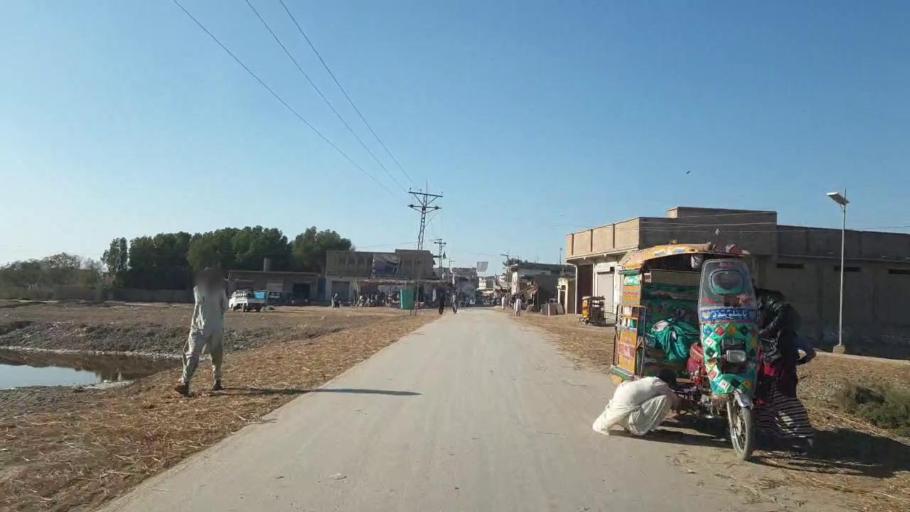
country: PK
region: Sindh
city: New Badah
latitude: 27.3270
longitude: 68.0290
